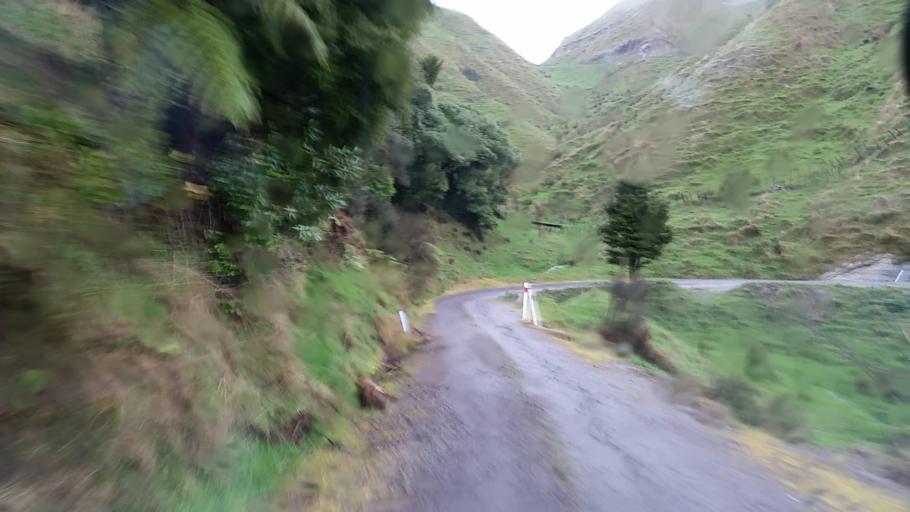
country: NZ
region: Taranaki
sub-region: South Taranaki District
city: Eltham
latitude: -39.4724
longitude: 174.4180
